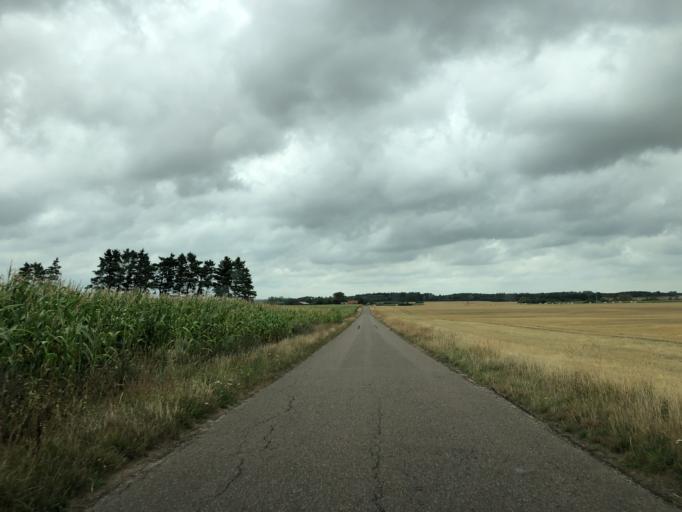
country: DK
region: Central Jutland
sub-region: Ringkobing-Skjern Kommune
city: Skjern
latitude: 56.0912
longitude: 8.4780
